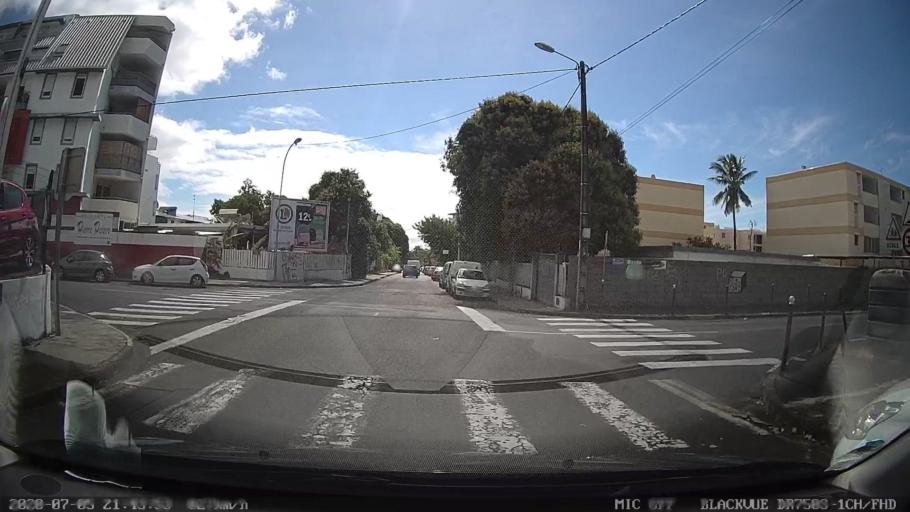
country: RE
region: Reunion
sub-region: Reunion
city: Saint-Denis
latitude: -20.8891
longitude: 55.4799
